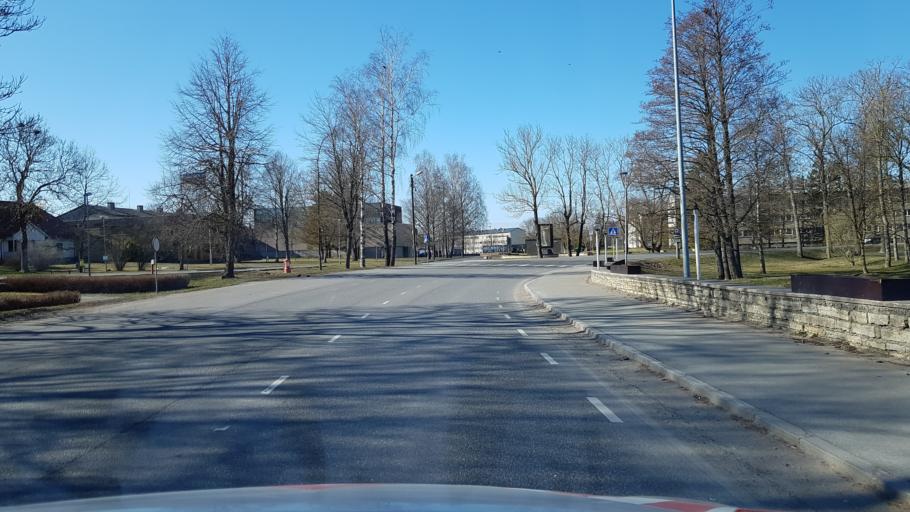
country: EE
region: Laeaene-Virumaa
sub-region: Haljala vald
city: Haljala
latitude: 59.4298
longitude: 26.2664
